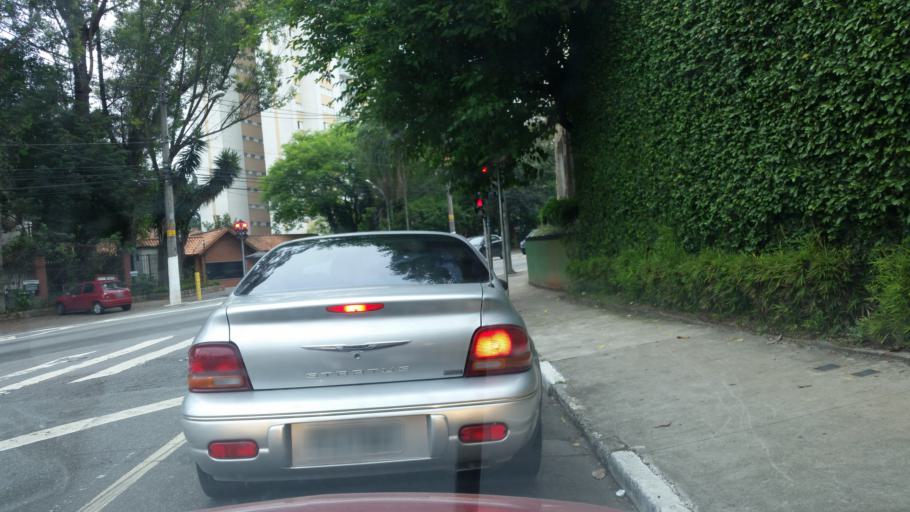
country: BR
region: Sao Paulo
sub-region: Diadema
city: Diadema
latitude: -23.6548
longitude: -46.6910
